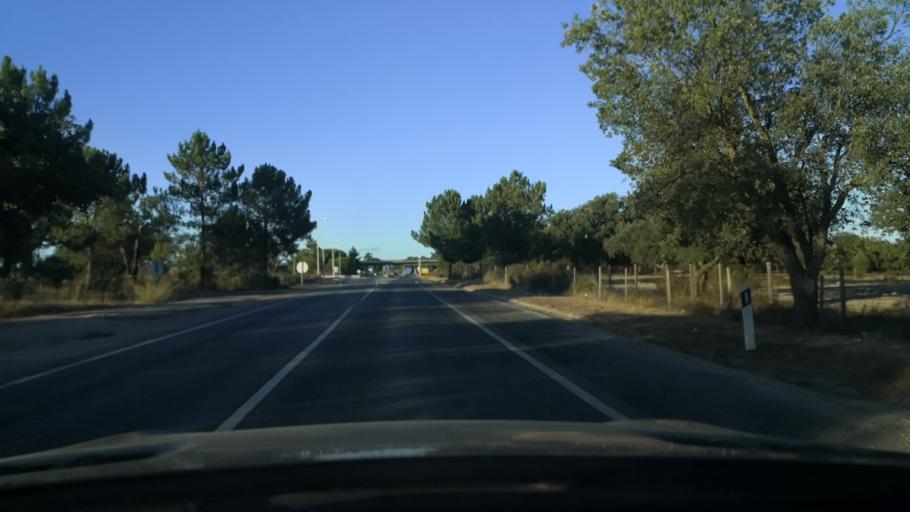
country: PT
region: Setubal
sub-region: Setubal
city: Setubal
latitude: 38.5920
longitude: -8.6746
